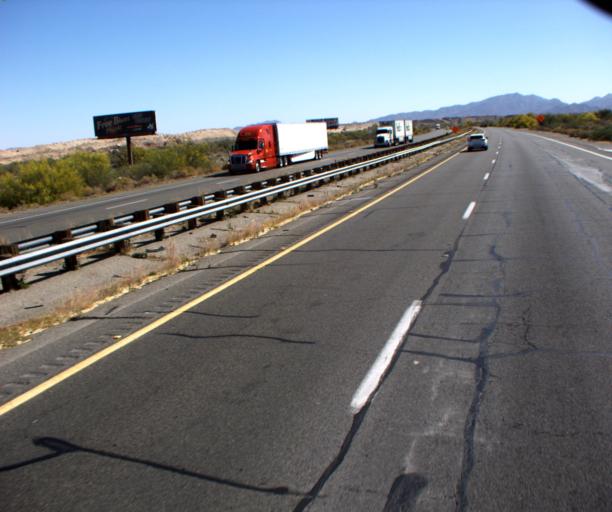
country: US
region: Arizona
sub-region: La Paz County
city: Ehrenberg
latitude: 33.6024
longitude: -114.5130
